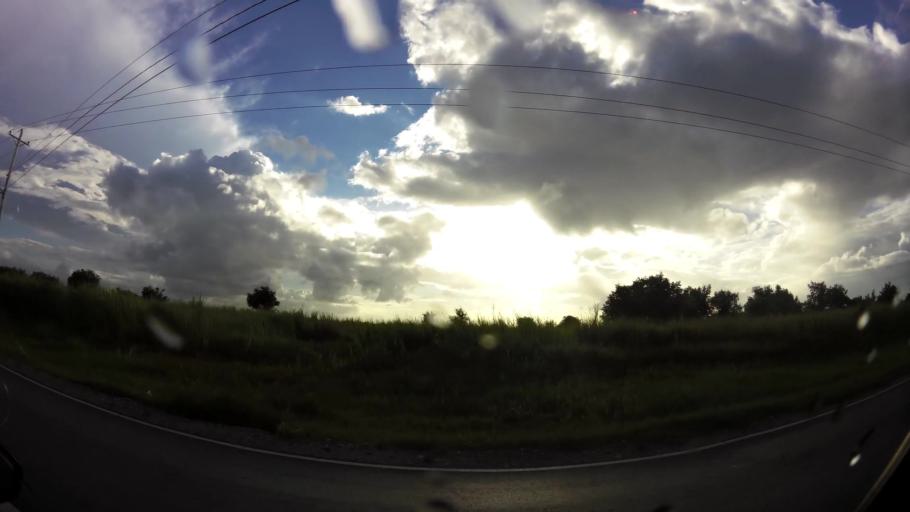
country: TT
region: Tunapuna/Piarco
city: Tunapuna
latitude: 10.5962
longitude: -61.3682
